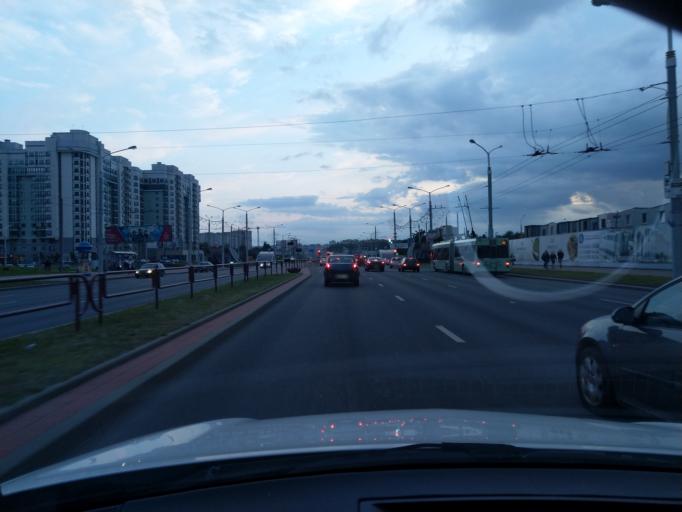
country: BY
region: Minsk
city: Minsk
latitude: 53.8875
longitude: 27.5168
